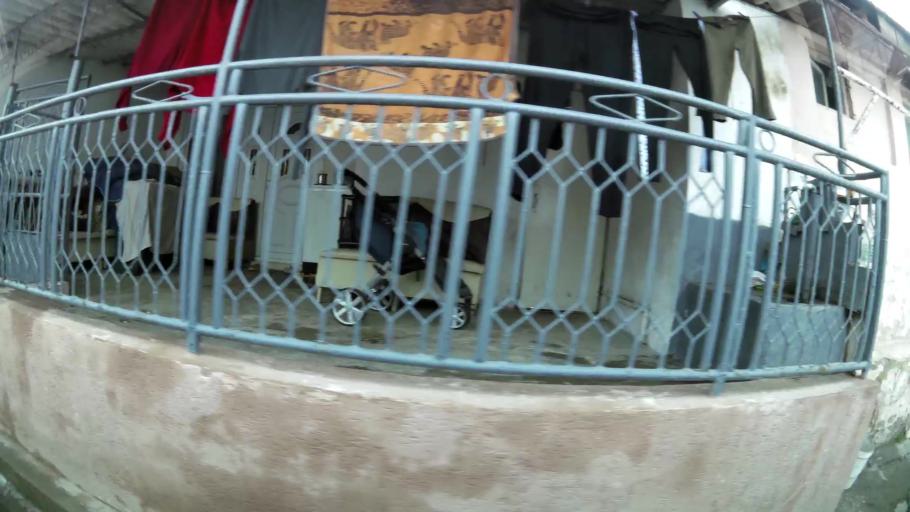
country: MK
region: Suto Orizari
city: Suto Orizare
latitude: 42.0397
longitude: 21.4214
